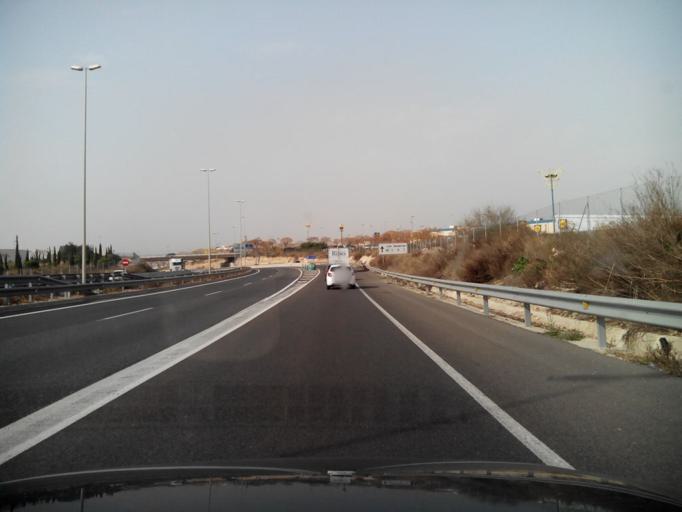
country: ES
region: Catalonia
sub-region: Provincia de Tarragona
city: Constanti
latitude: 41.1319
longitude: 1.2097
